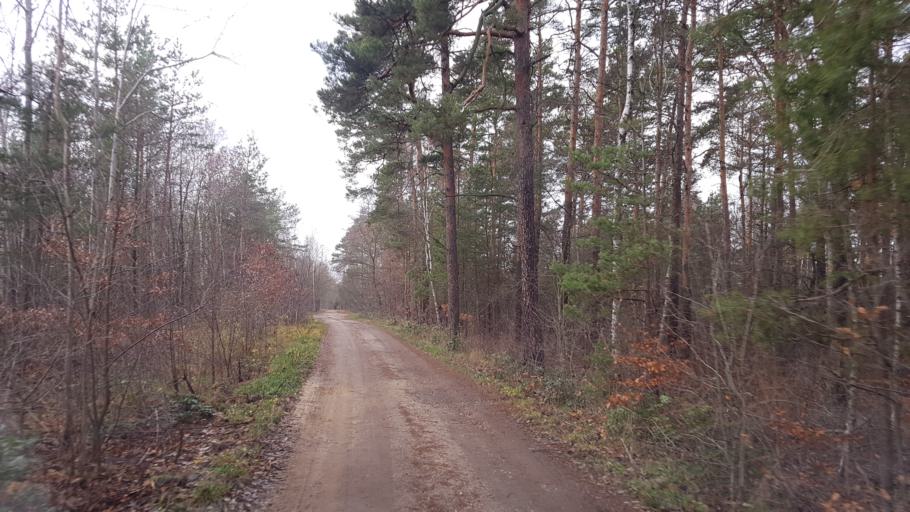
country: DE
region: Brandenburg
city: Sallgast
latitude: 51.5863
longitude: 13.8226
